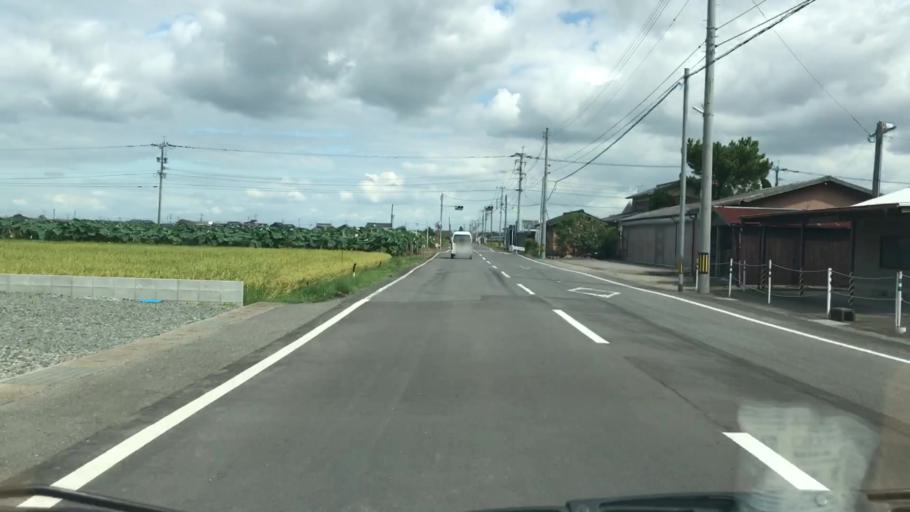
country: JP
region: Saga Prefecture
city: Saga-shi
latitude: 33.1956
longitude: 130.1861
